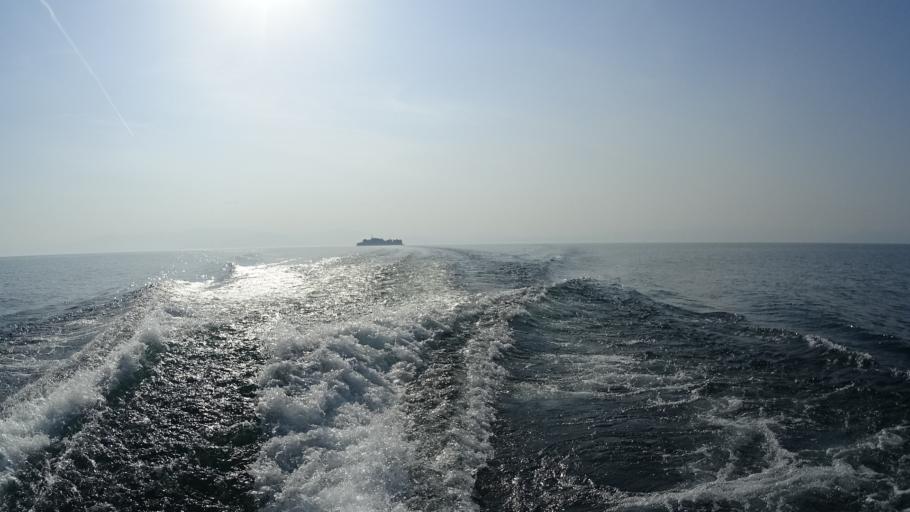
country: JP
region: Shiga Prefecture
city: Hikone
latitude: 35.2935
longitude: 136.1987
